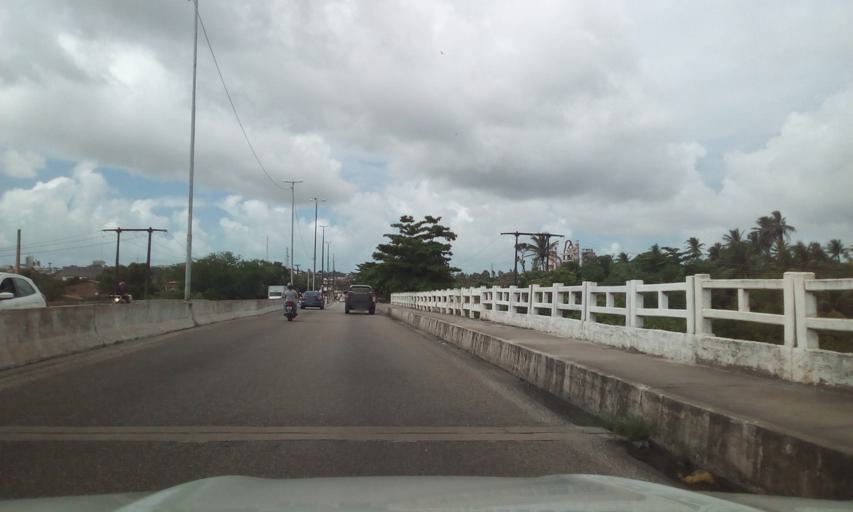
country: BR
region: Paraiba
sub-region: Bayeux
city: Bayeux
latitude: -7.1224
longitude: -34.9014
